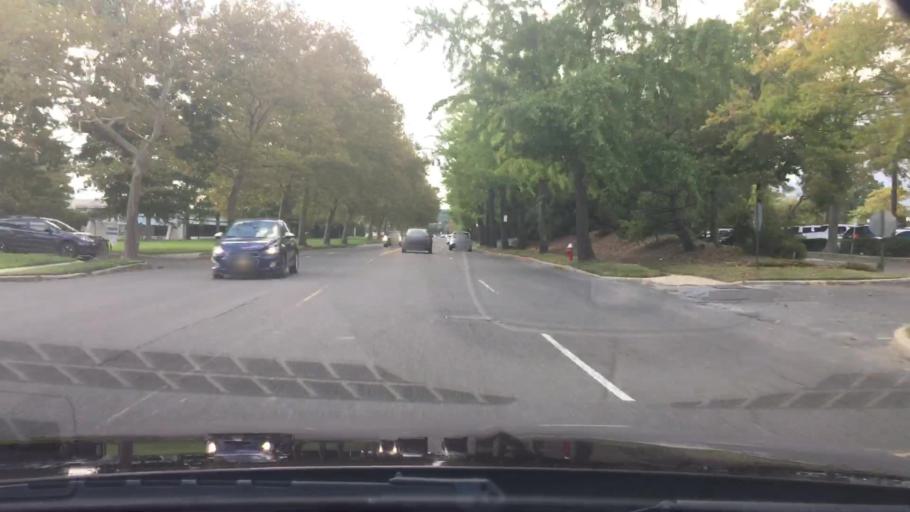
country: US
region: New York
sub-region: Suffolk County
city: Melville
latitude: 40.7705
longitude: -73.4160
